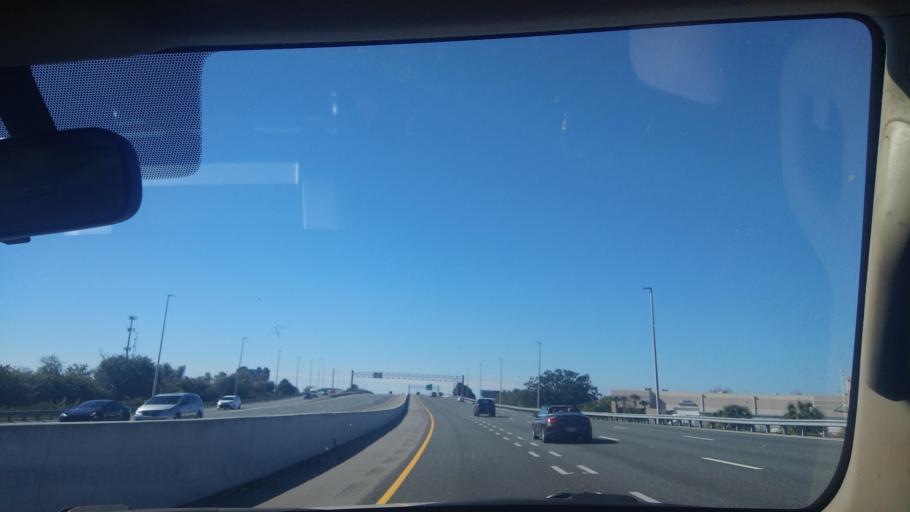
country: US
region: Florida
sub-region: Orange County
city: Sky Lake
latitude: 28.4415
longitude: -81.3962
